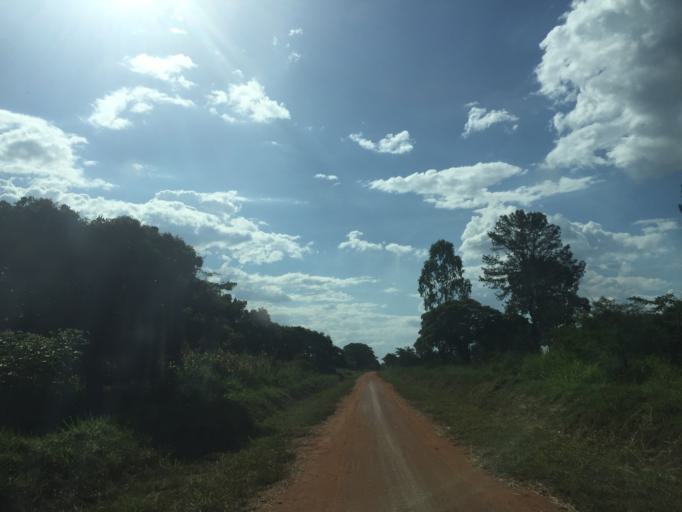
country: UG
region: Western Region
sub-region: Kiryandongo District
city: Masindi Port
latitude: 1.5282
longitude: 32.0952
